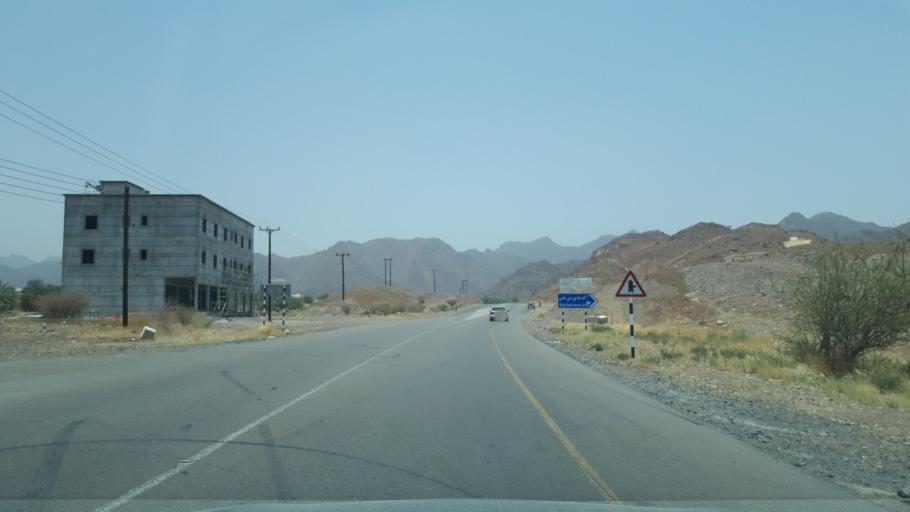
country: OM
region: Al Batinah
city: Rustaq
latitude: 23.4257
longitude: 57.2863
